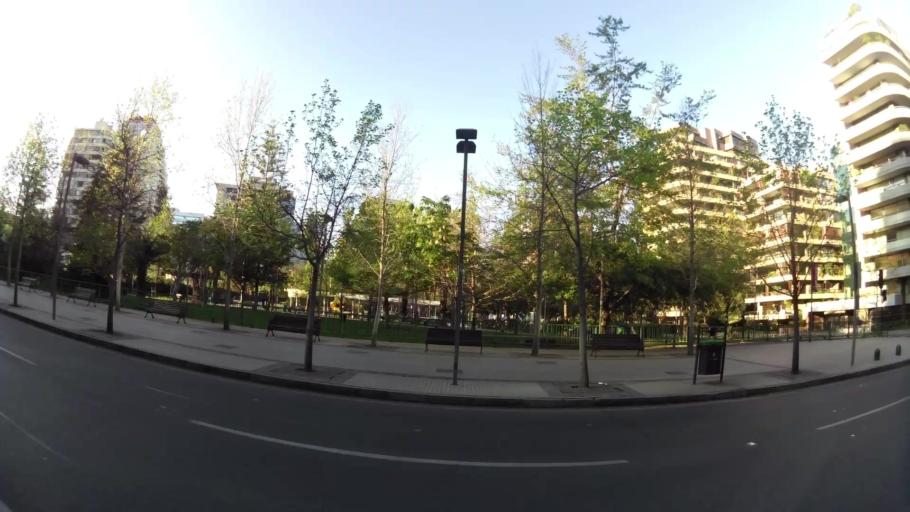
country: CL
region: Santiago Metropolitan
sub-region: Provincia de Santiago
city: Villa Presidente Frei, Nunoa, Santiago, Chile
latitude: -33.4144
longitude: -70.5987
